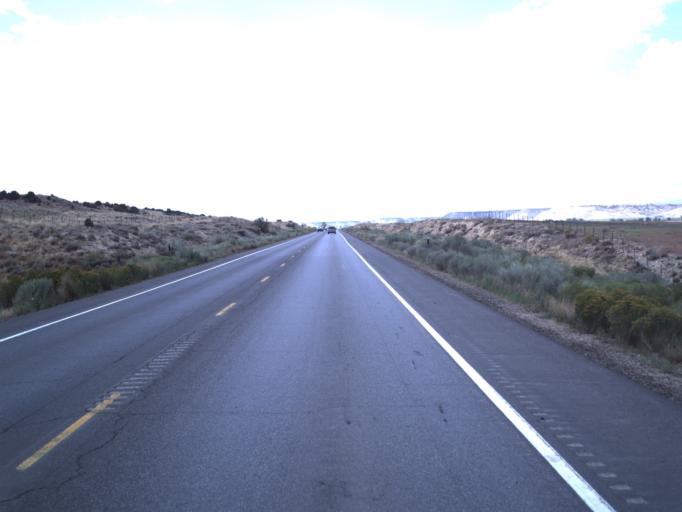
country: US
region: Utah
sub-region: Duchesne County
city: Duchesne
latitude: 40.1652
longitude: -110.2869
